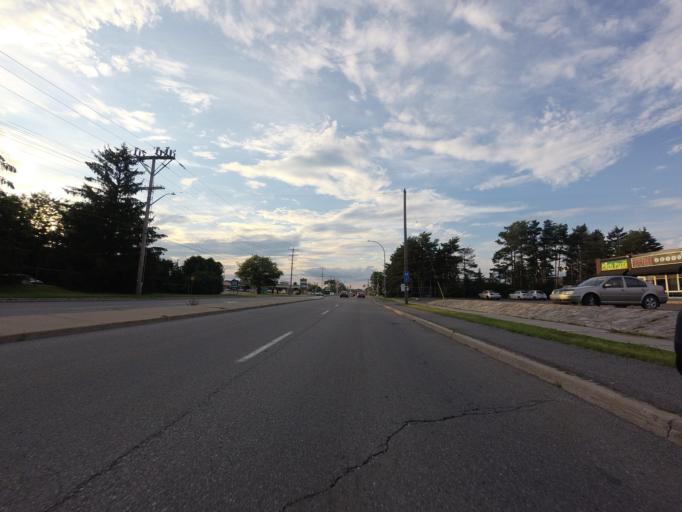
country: CA
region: Ontario
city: Bells Corners
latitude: 45.3241
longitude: -75.7781
